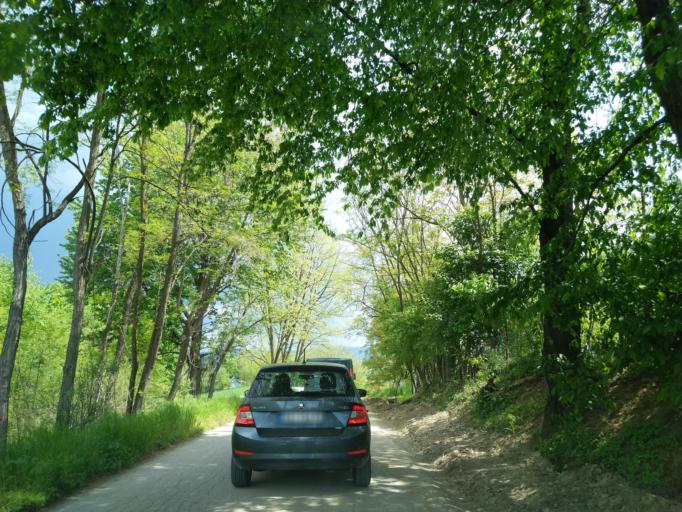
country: RS
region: Central Serbia
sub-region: Zlatiborski Okrug
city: Uzice
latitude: 43.8621
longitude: 19.9352
